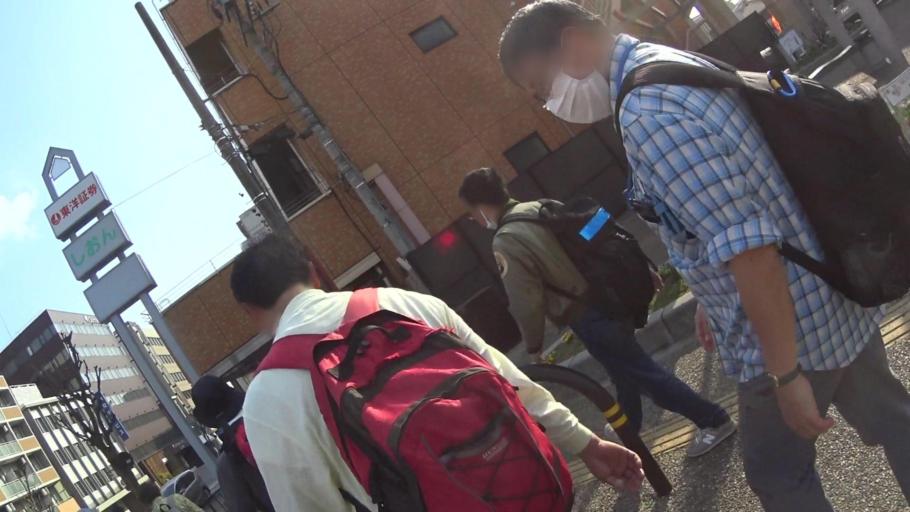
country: JP
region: Nara
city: Nara-shi
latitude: 34.6842
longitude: 135.8202
